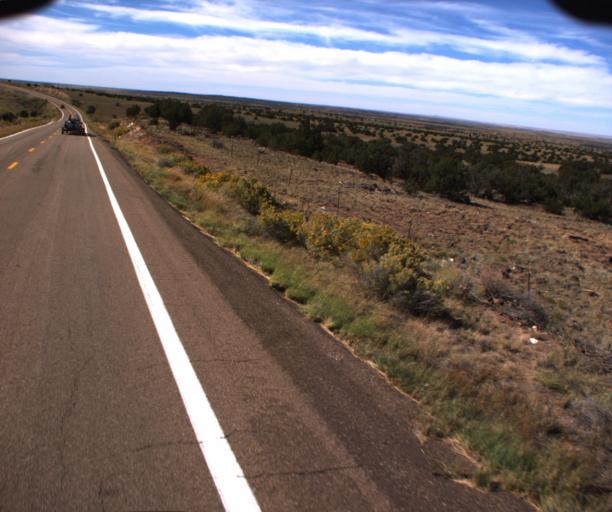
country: US
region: Arizona
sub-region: Apache County
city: Saint Johns
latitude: 34.4845
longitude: -109.5741
